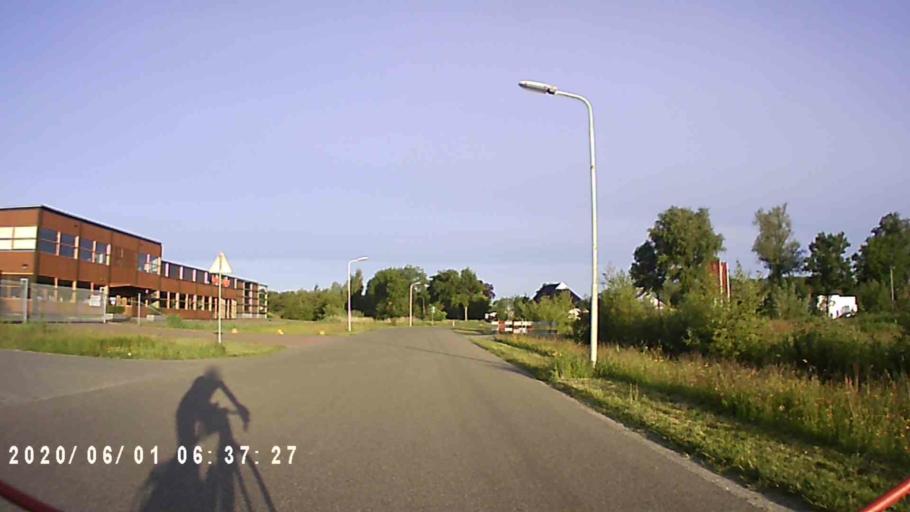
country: NL
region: Friesland
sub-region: Gemeente Kollumerland en Nieuwkruisland
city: Kollum
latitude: 53.2846
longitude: 6.1601
